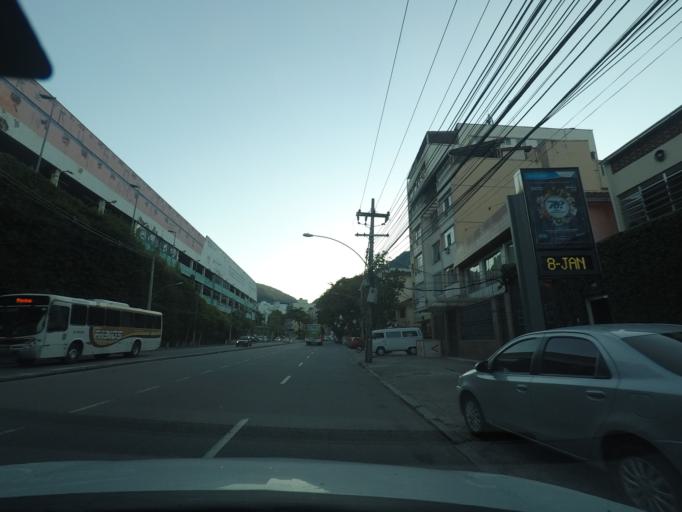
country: BR
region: Rio de Janeiro
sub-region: Rio De Janeiro
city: Rio de Janeiro
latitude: -22.9416
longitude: -43.2525
